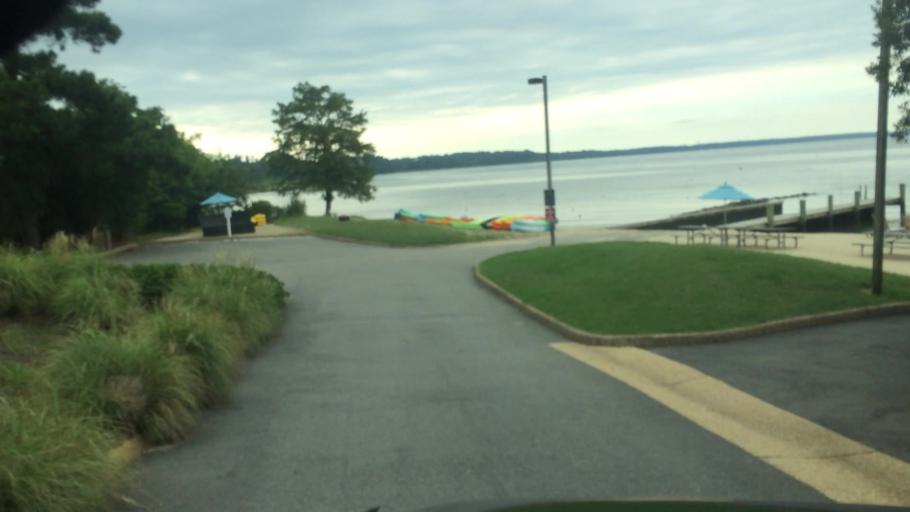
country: US
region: Virginia
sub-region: City of Williamsburg
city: Williamsburg
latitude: 37.2231
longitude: -76.6626
